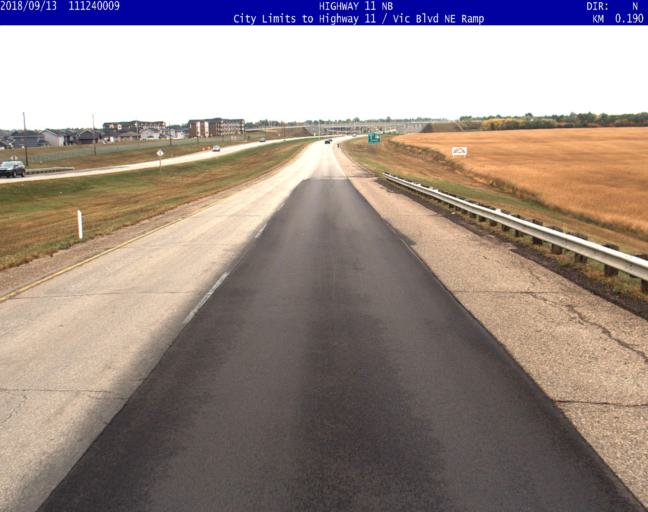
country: CA
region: Saskatchewan
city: Saskatoon
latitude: 52.0715
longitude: -106.6034
